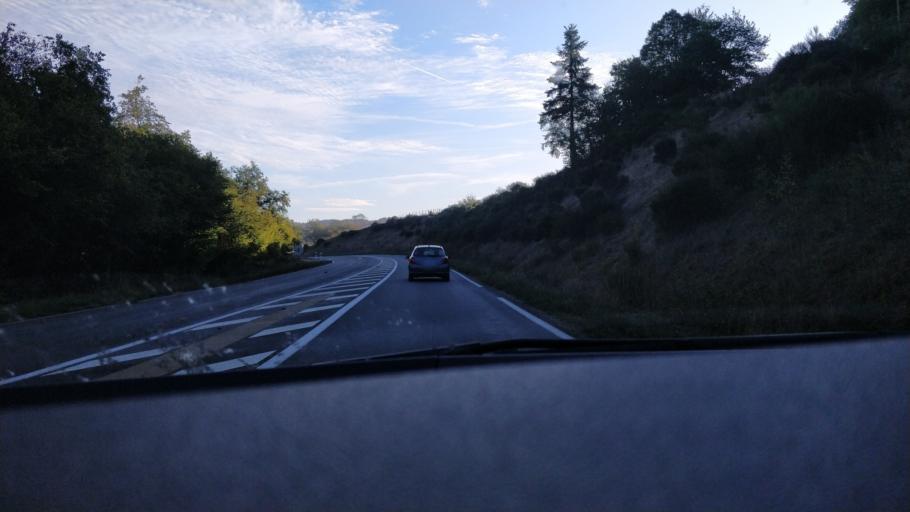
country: FR
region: Limousin
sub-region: Departement de la Creuse
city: Bourganeuf
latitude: 45.9530
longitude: 1.7272
